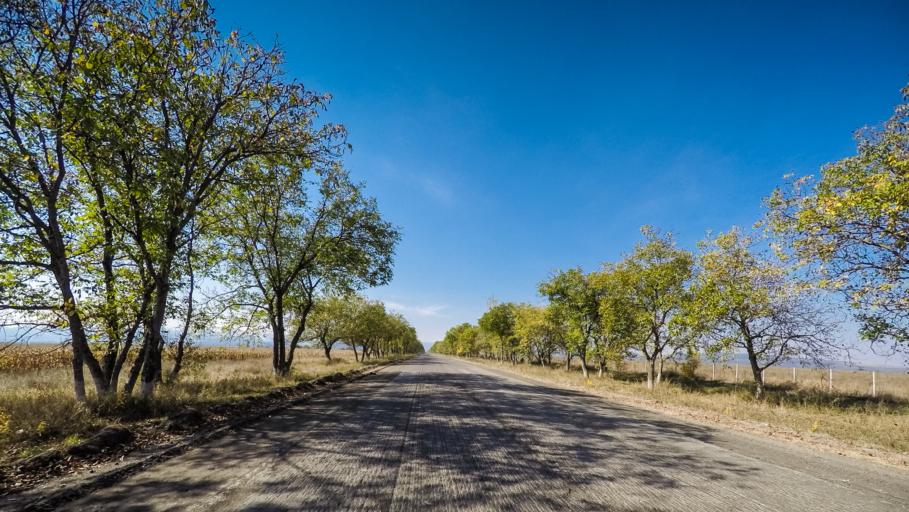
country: RU
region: Kabardino-Balkariya
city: Kamenka
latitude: 43.5703
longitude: 43.5197
